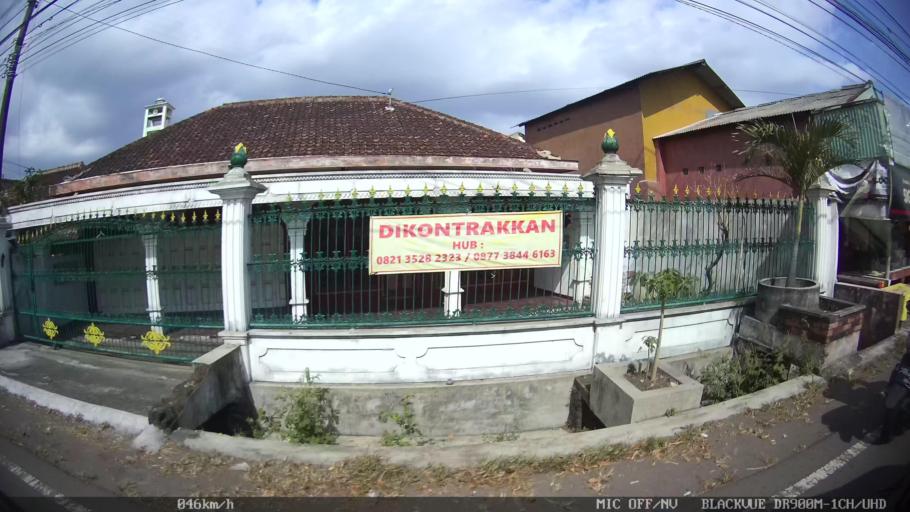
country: ID
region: Daerah Istimewa Yogyakarta
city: Gamping Lor
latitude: -7.7715
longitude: 110.3337
